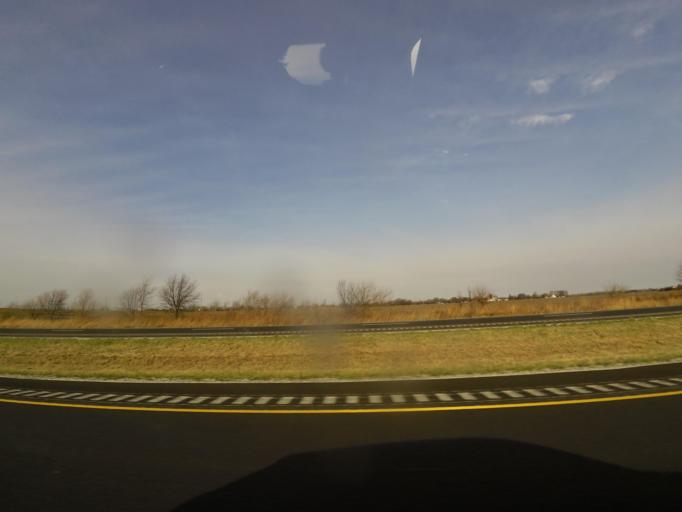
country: US
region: Illinois
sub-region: Macon County
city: Macon
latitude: 39.7668
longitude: -88.9777
